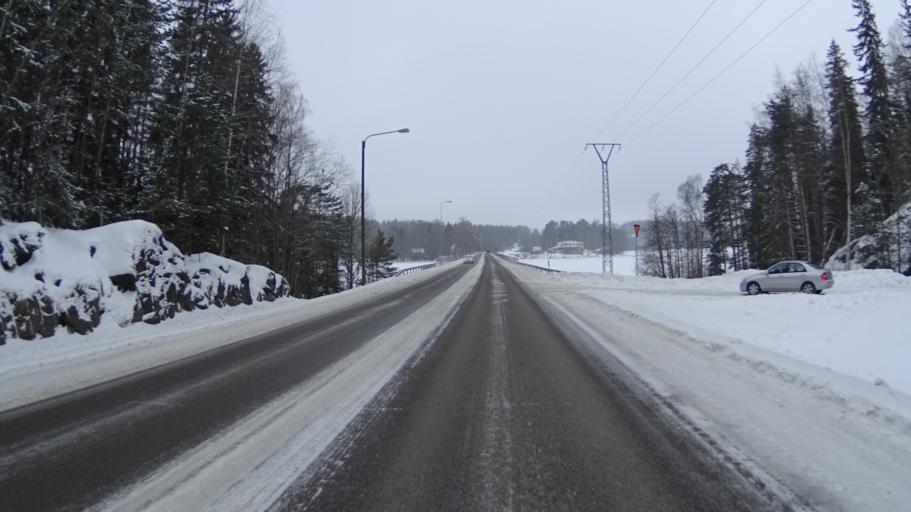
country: FI
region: Uusimaa
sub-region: Helsinki
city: Lohja
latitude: 60.3601
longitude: 24.1731
